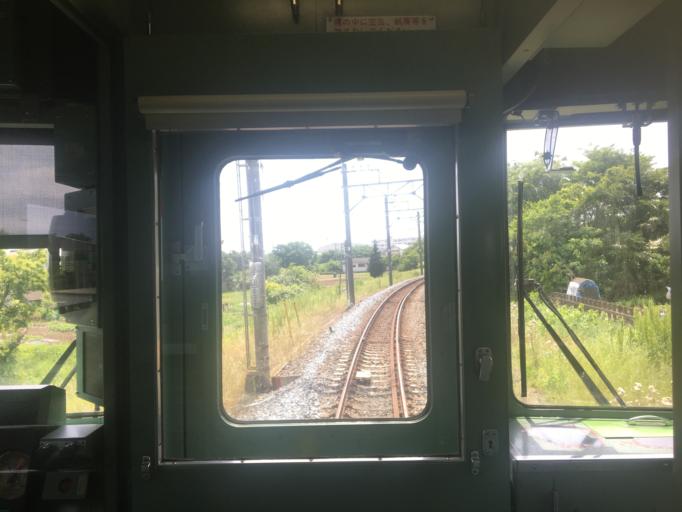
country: JP
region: Saitama
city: Morohongo
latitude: 35.9371
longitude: 139.3481
